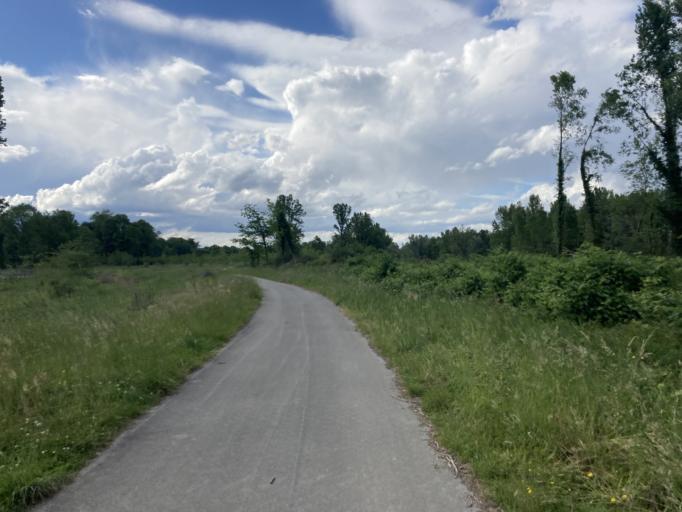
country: FR
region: Aquitaine
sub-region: Departement des Pyrenees-Atlantiques
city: Arbus
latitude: 43.3448
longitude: -0.5059
